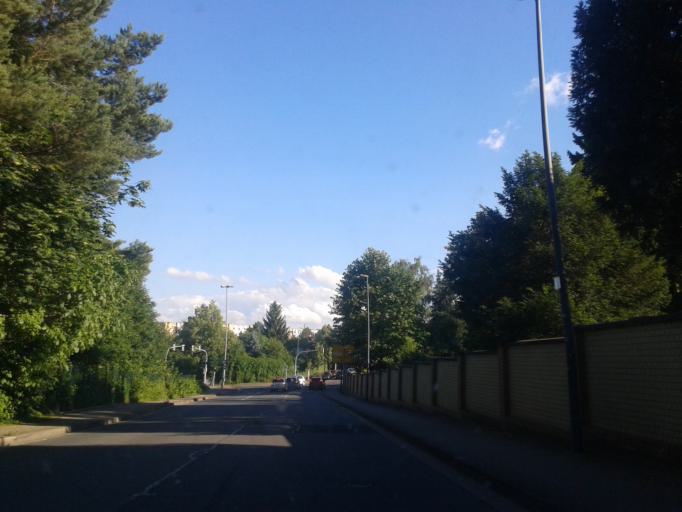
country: DE
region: Saxony
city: Freital
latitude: 51.0513
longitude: 13.6722
